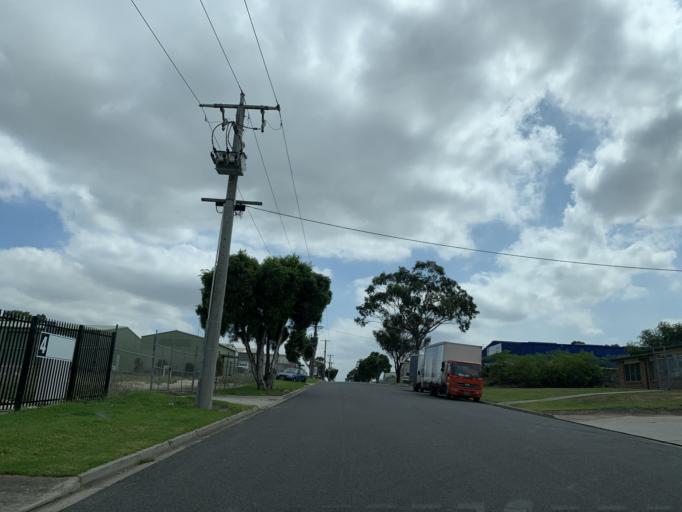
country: AU
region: Victoria
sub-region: Latrobe
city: Traralgon
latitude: -38.1907
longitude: 146.5681
